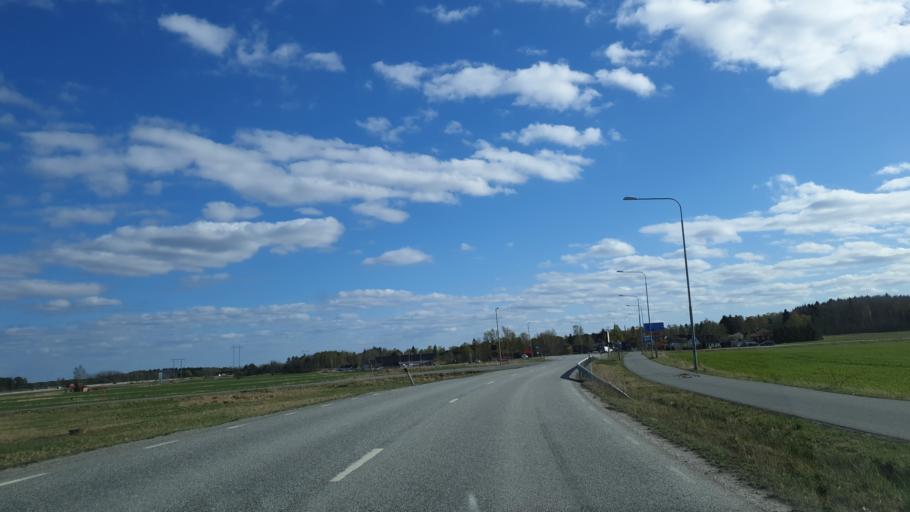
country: SE
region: Stockholm
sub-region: Sigtuna Kommun
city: Rosersberg
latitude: 59.5922
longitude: 17.8908
